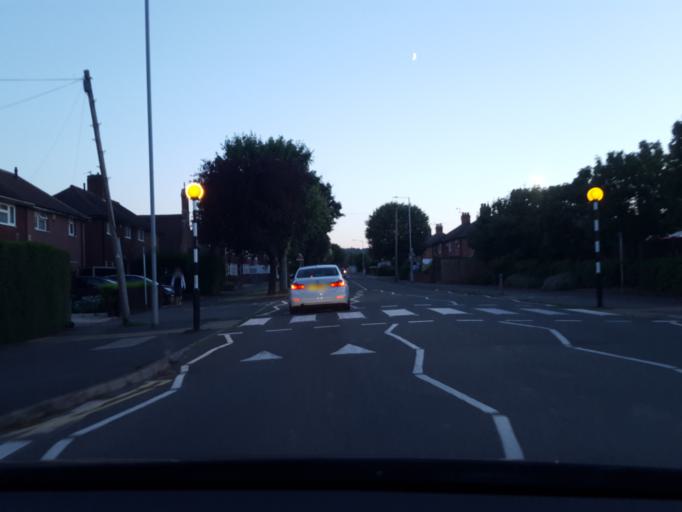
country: GB
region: England
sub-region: Leicestershire
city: Loughborough
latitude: 52.7578
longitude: -1.2079
